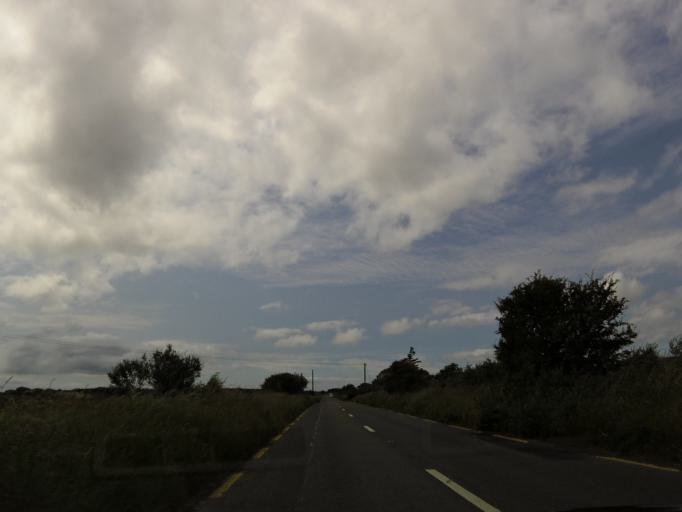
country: IE
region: Munster
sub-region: An Clar
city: Kilrush
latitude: 52.6722
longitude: -9.5736
